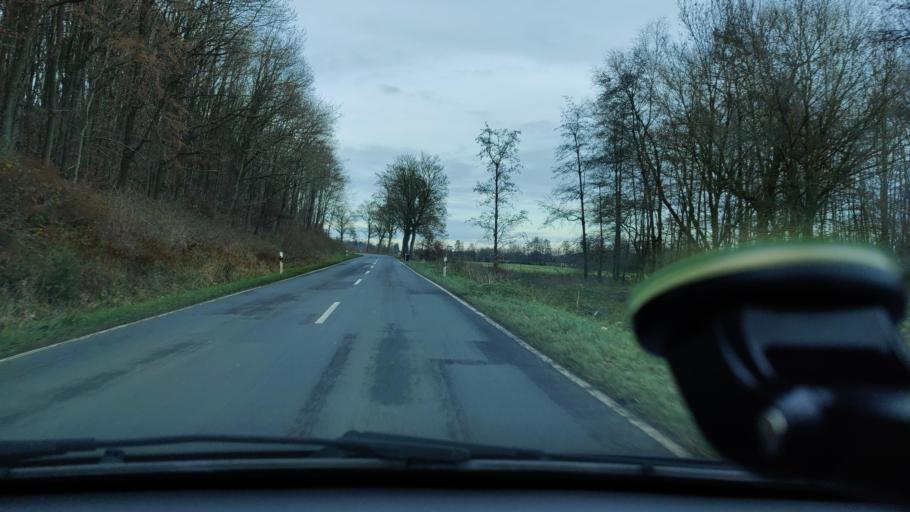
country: DE
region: North Rhine-Westphalia
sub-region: Regierungsbezirk Dusseldorf
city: Sonsbeck
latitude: 51.6804
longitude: 6.3797
